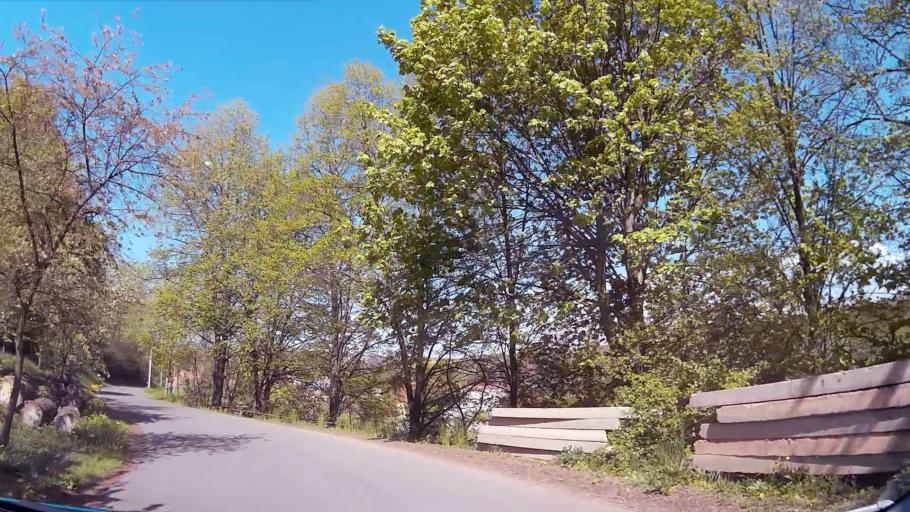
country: CZ
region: South Moravian
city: Moravsky Krumlov
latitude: 49.0834
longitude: 16.3216
